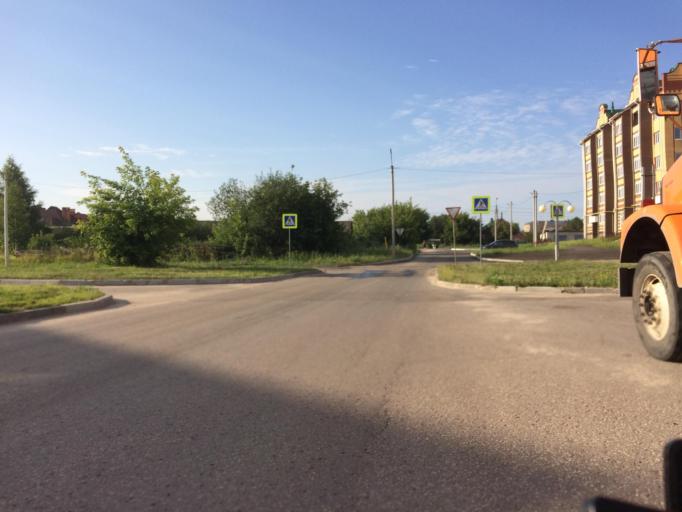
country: RU
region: Mariy-El
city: Medvedevo
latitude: 56.6362
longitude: 47.8122
